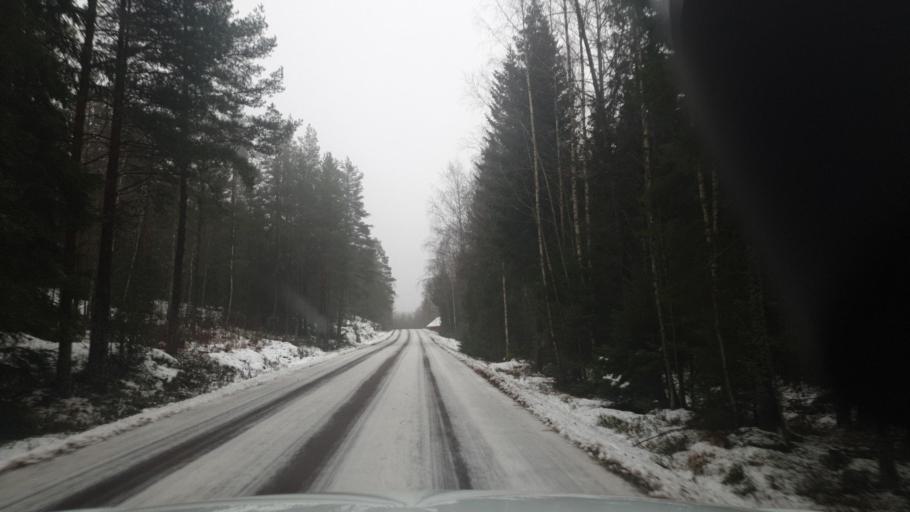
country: SE
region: Vaermland
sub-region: Karlstads Kommun
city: Valberg
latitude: 59.4540
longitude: 13.0876
